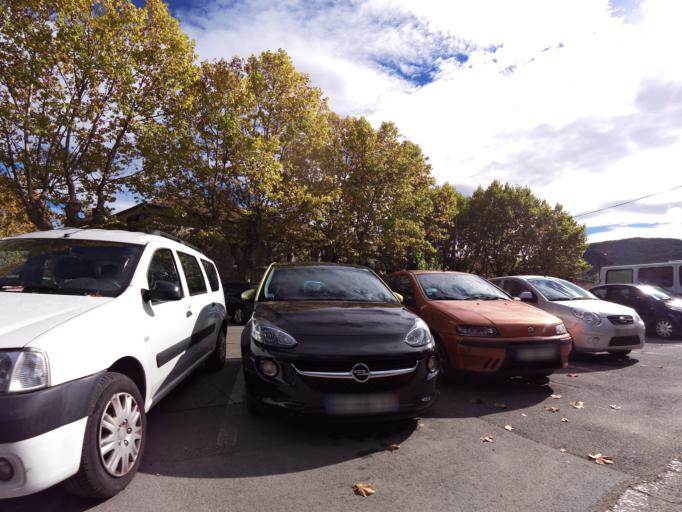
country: FR
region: Languedoc-Roussillon
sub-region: Departement du Gard
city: Saint-Hippolyte-du-Fort
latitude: 43.9654
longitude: 3.8539
